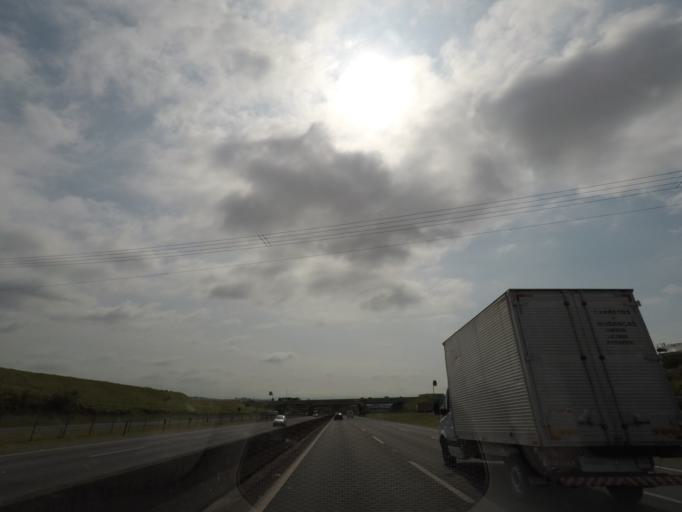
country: BR
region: Sao Paulo
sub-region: Campinas
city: Campinas
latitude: -22.8442
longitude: -47.0406
